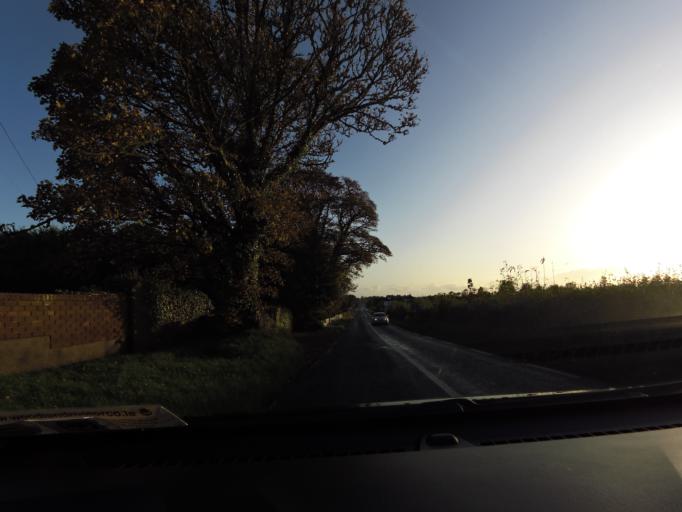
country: IE
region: Connaught
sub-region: Roscommon
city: Castlerea
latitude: 53.7359
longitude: -8.5510
